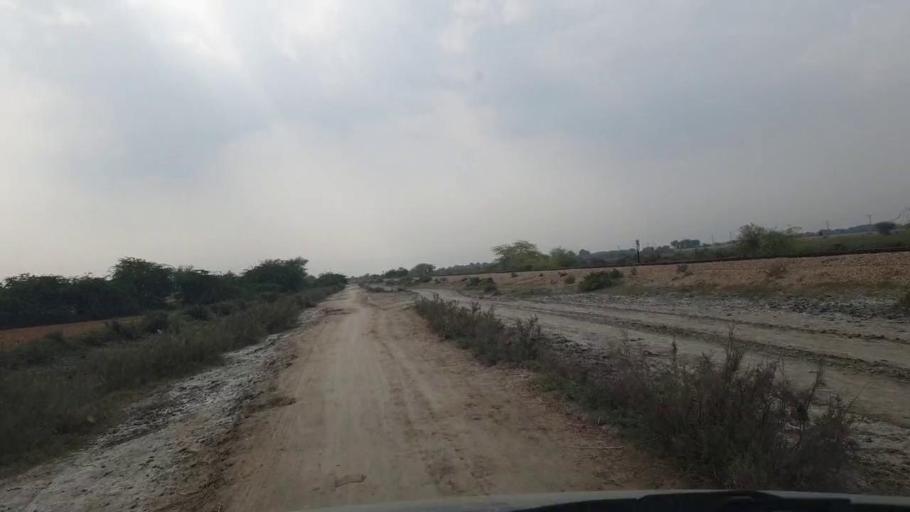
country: PK
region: Sindh
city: Talhar
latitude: 24.8620
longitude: 68.8186
